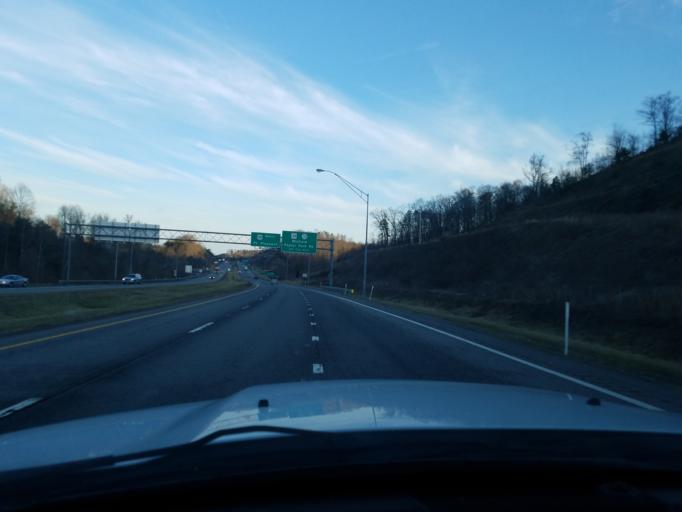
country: US
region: West Virginia
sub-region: Putnam County
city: Teays Valley
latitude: 38.4589
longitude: -81.9047
